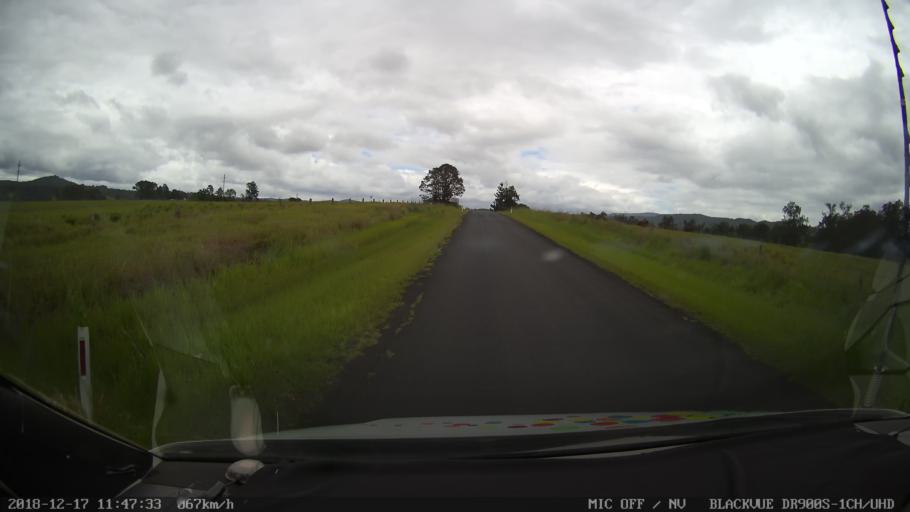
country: AU
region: New South Wales
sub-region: Kyogle
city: Kyogle
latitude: -28.6261
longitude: 152.5913
